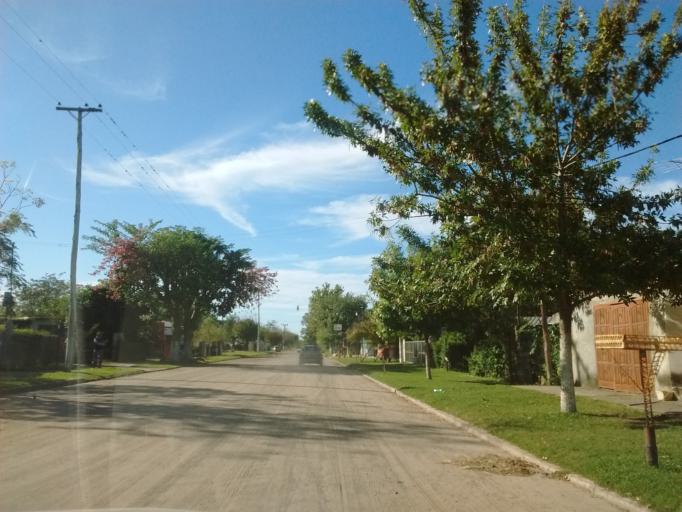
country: AR
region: Santa Fe
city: Coronda
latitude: -32.2440
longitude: -60.9209
